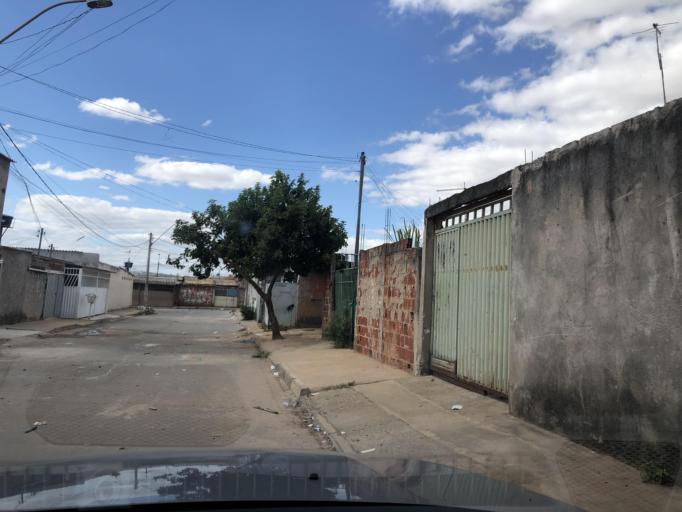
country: BR
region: Federal District
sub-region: Brasilia
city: Brasilia
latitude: -15.8869
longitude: -48.1456
